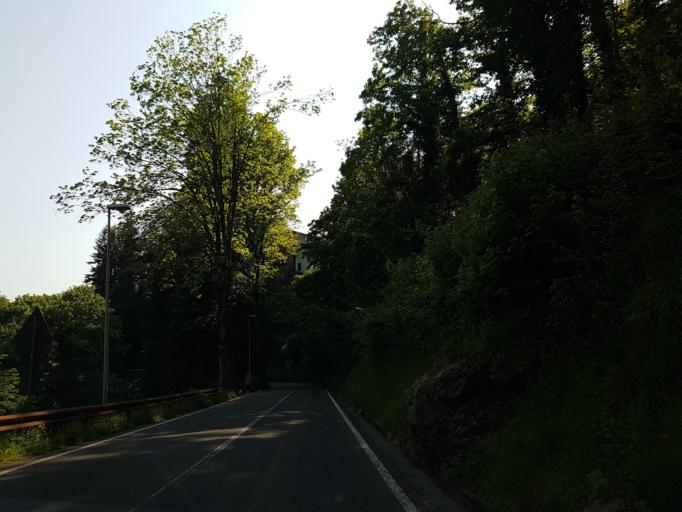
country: IT
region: Tuscany
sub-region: Province of Arezzo
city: Soci
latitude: 43.7952
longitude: 11.8827
